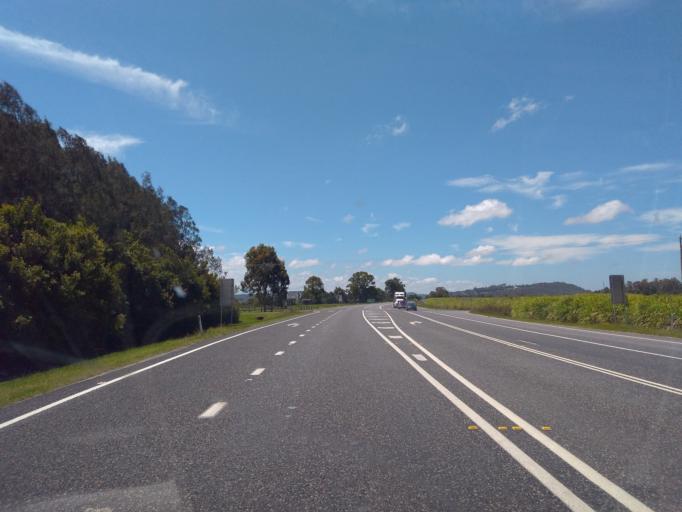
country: AU
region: New South Wales
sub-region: Clarence Valley
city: Maclean
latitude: -29.5024
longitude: 153.1948
